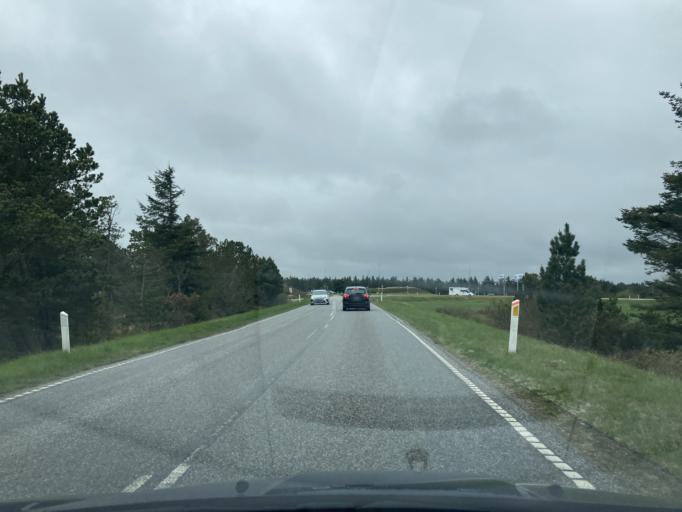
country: DK
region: North Denmark
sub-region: Thisted Kommune
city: Hurup
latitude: 56.9213
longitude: 8.3735
